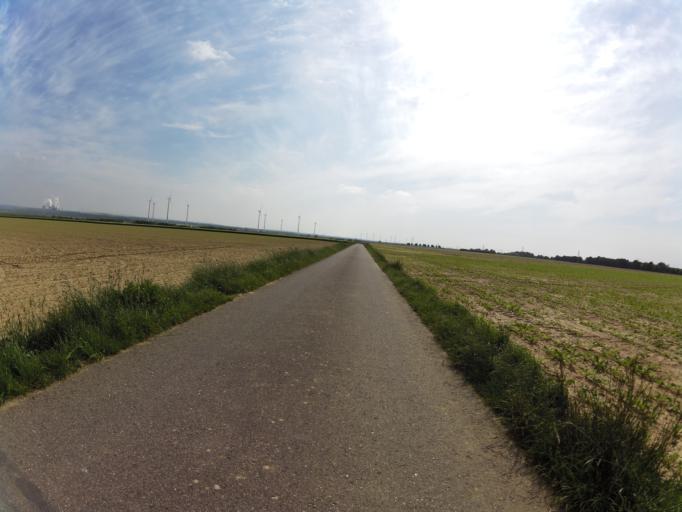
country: DE
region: North Rhine-Westphalia
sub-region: Regierungsbezirk Koln
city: Aldenhoven
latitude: 50.8981
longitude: 6.3103
